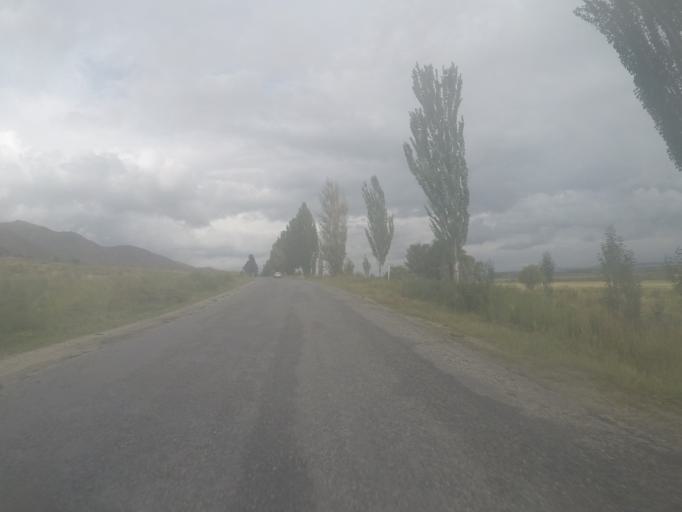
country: KG
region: Ysyk-Koel
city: Tyup
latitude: 42.7418
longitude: 78.0605
